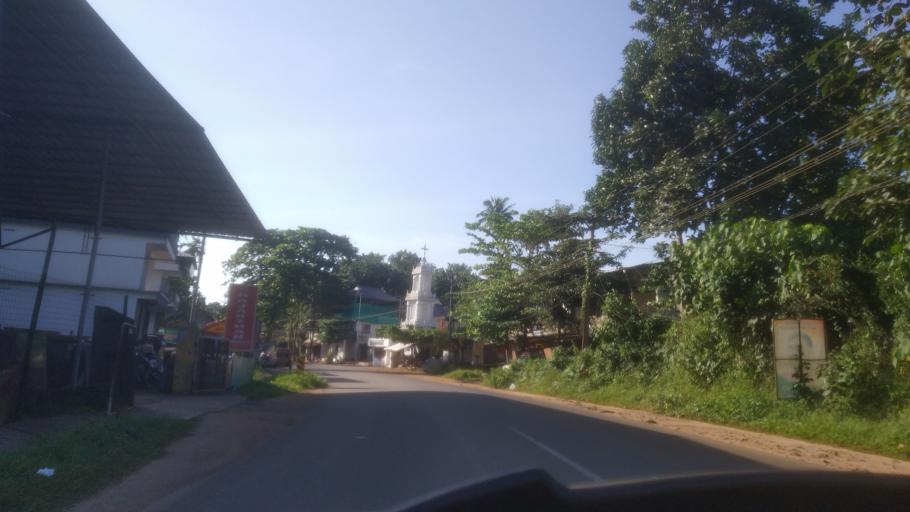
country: IN
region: Kerala
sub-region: Ernakulam
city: Ramamangalam
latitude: 9.9764
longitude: 76.4983
